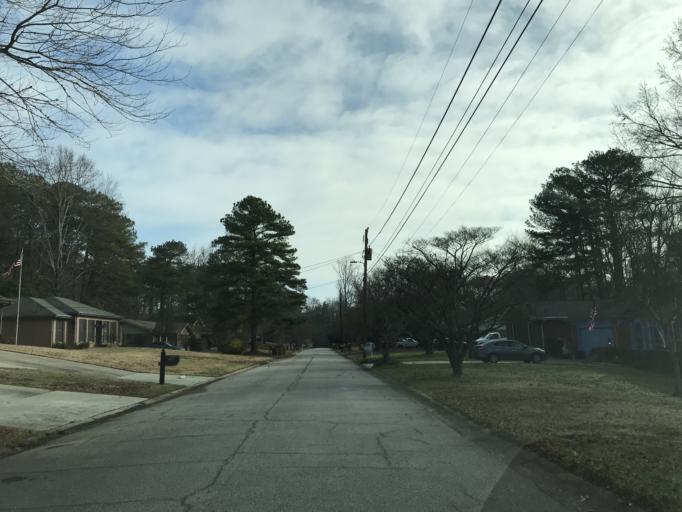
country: US
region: Georgia
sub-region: Clayton County
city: Morrow
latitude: 33.5627
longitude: -84.3664
